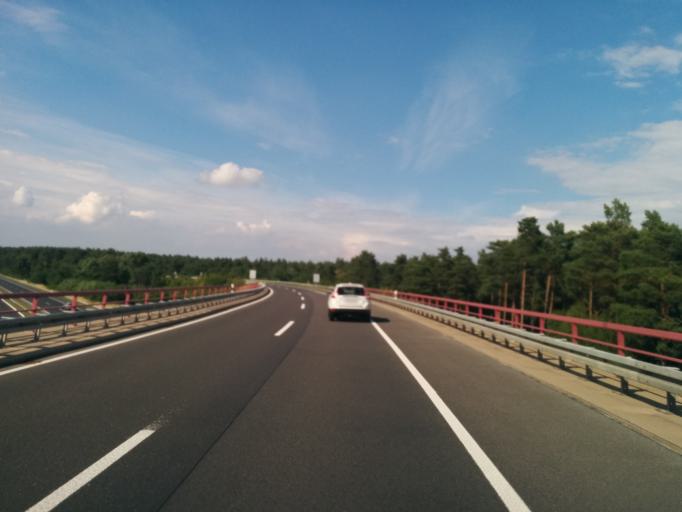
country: DE
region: Brandenburg
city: Gross Kreutz
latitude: 52.3394
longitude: 12.8158
